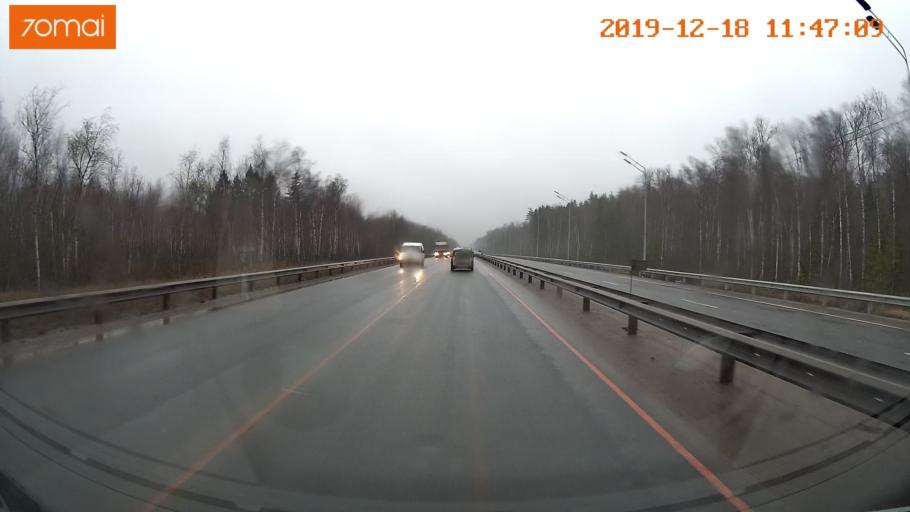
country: RU
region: Moskovskaya
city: Yershovo
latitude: 55.7549
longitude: 36.8922
